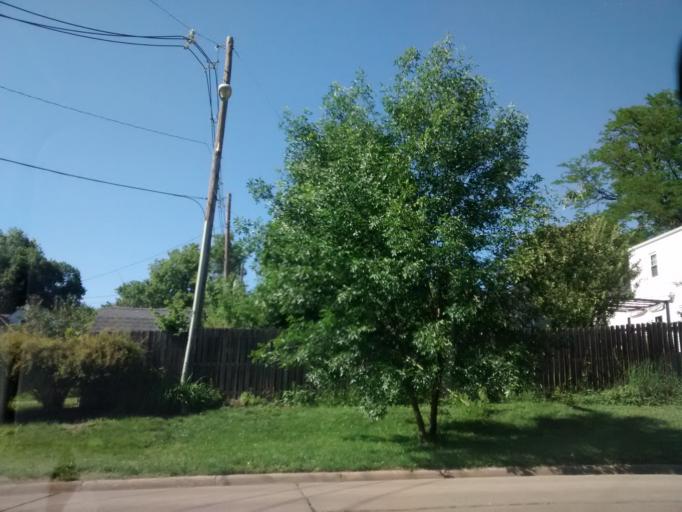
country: US
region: Nebraska
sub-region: Douglas County
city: Ralston
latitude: 41.2560
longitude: -96.0200
